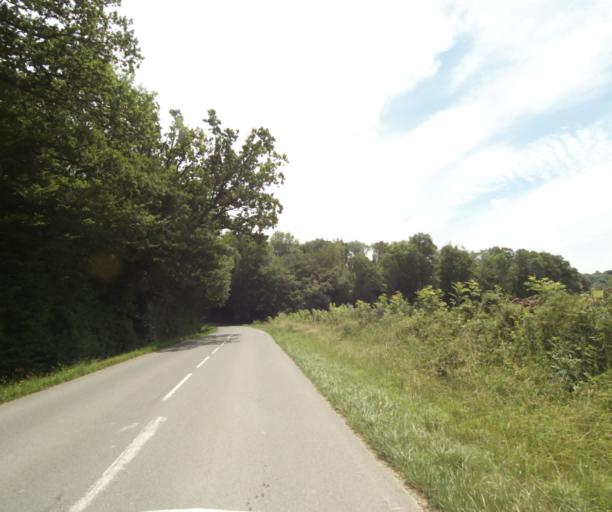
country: FR
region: Rhone-Alpes
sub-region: Departement de la Haute-Savoie
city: Allinges
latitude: 46.3464
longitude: 6.4536
